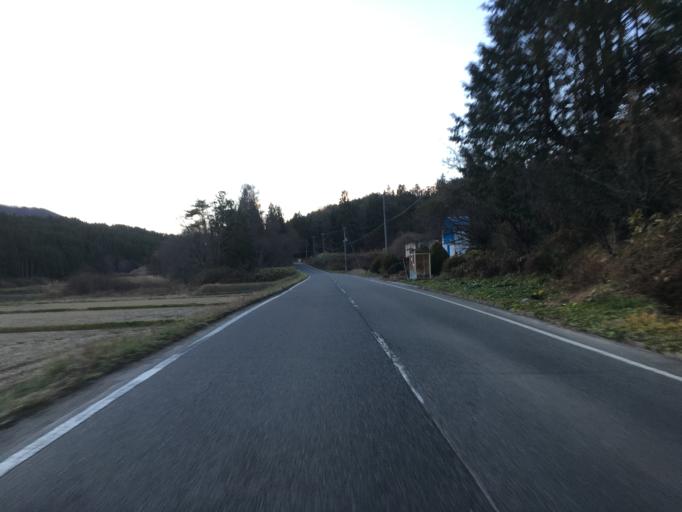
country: JP
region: Fukushima
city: Ishikawa
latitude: 37.2735
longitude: 140.5694
